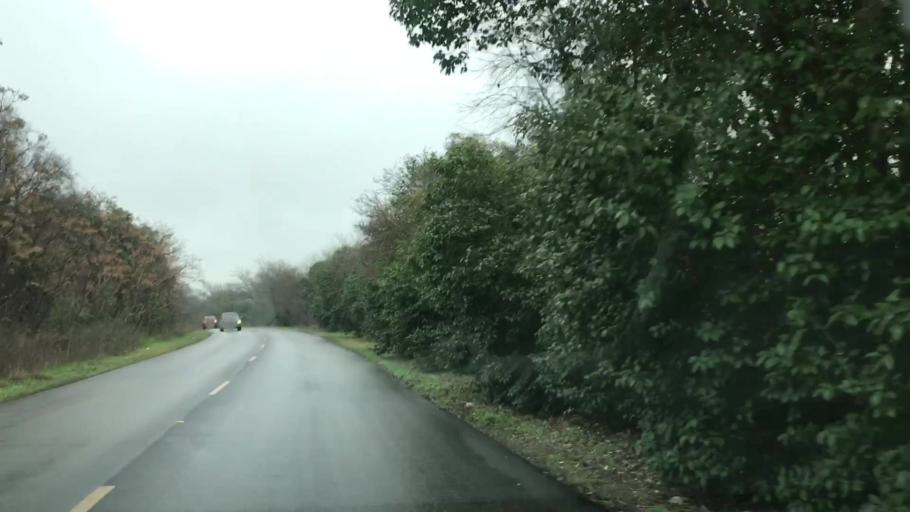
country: US
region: Texas
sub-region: Hays County
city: San Marcos
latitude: 29.8906
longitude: -97.9018
